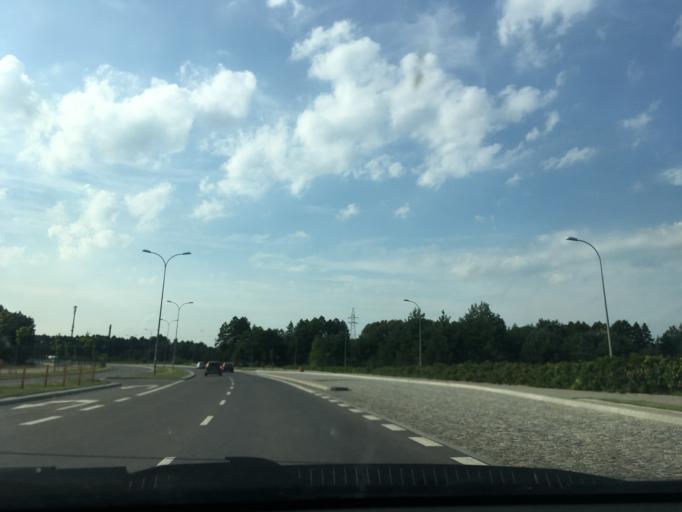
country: PL
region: Podlasie
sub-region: Bialystok
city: Bialystok
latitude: 53.1364
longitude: 23.2203
